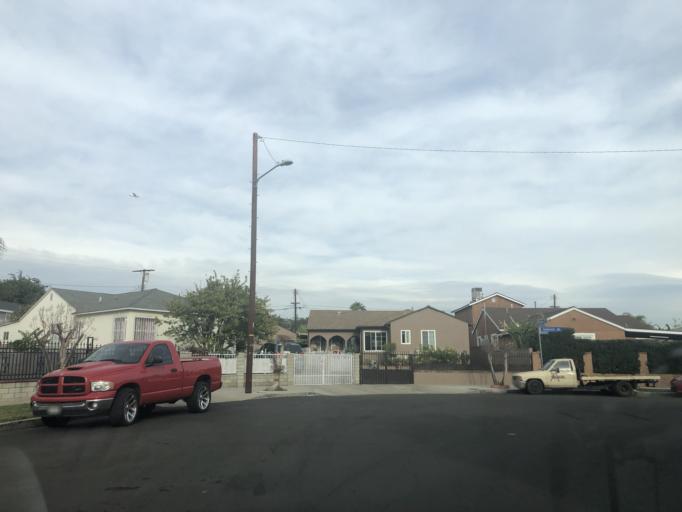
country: US
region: California
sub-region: Los Angeles County
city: San Fernando
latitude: 34.2689
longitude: -118.4299
